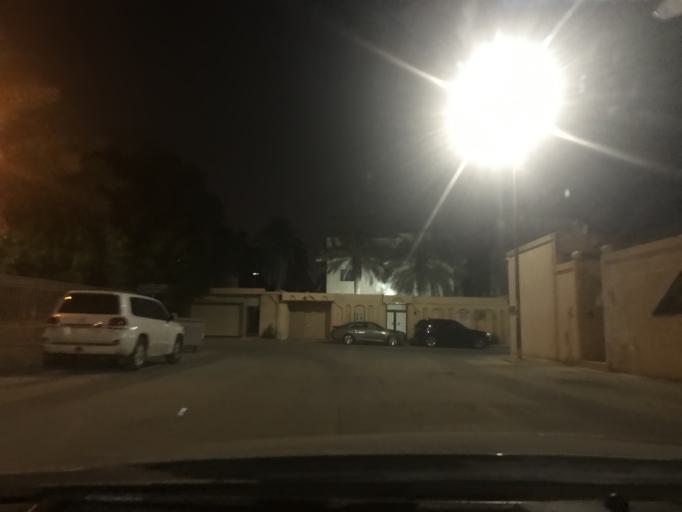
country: SA
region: Ar Riyad
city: Riyadh
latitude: 24.7397
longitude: 46.7618
